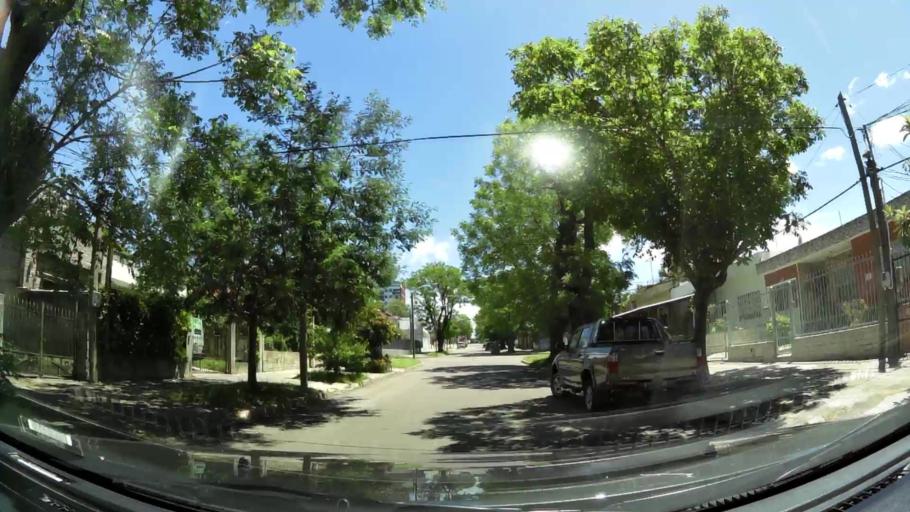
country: UY
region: Montevideo
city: Montevideo
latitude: -34.8919
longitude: -56.1336
